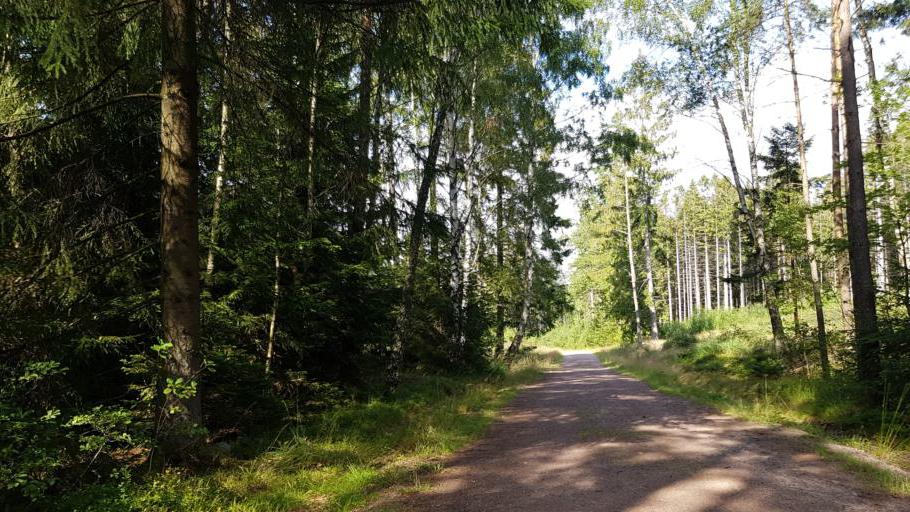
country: SE
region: Vaestra Goetaland
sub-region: Partille Kommun
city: Ojersjo
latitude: 57.6805
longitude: 12.0702
